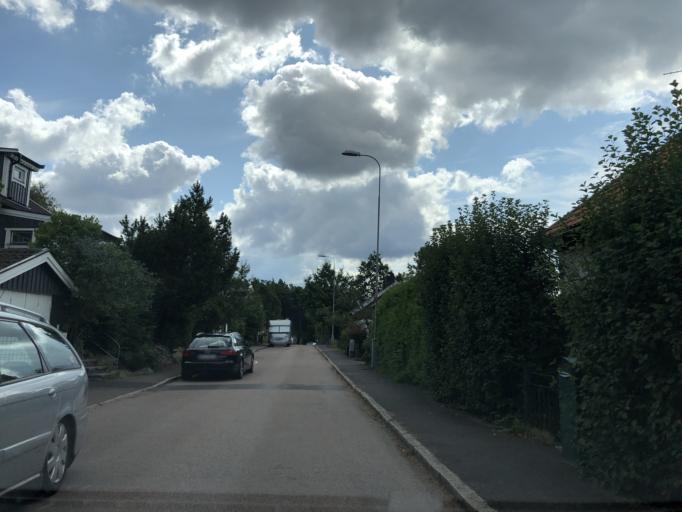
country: SE
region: Vaestra Goetaland
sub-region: Goteborg
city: Majorna
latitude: 57.7215
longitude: 11.9185
